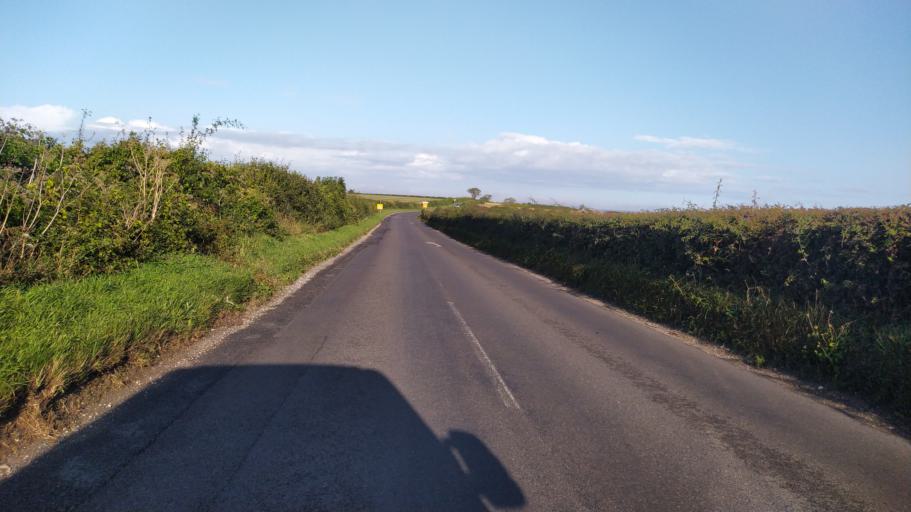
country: GB
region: England
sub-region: Wiltshire
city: Bower Chalke
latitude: 50.9005
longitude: -2.0266
